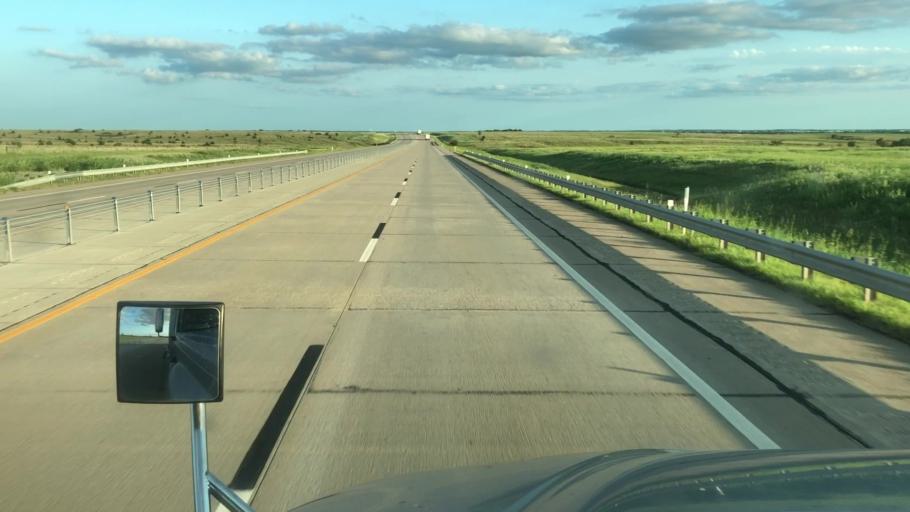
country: US
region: Oklahoma
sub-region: Pawnee County
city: Pawnee
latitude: 36.3553
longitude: -97.0312
